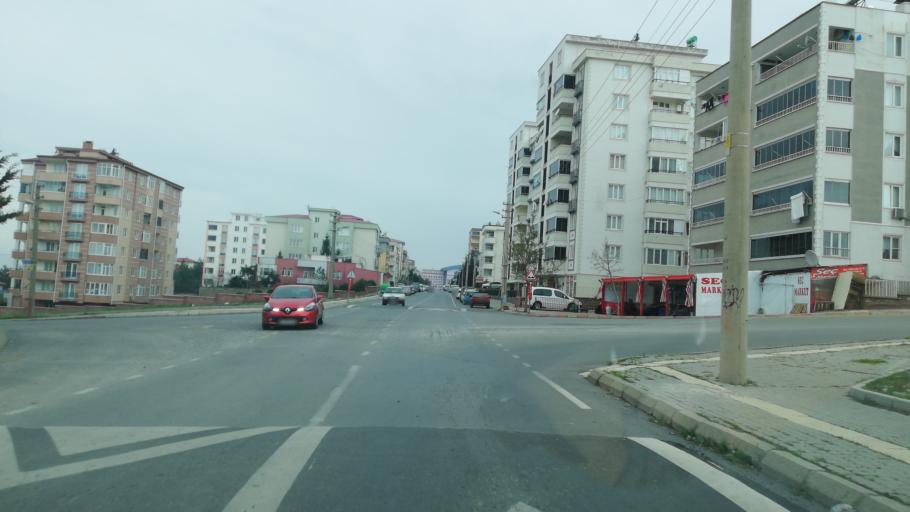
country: TR
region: Kahramanmaras
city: Kahramanmaras
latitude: 37.5932
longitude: 36.8907
